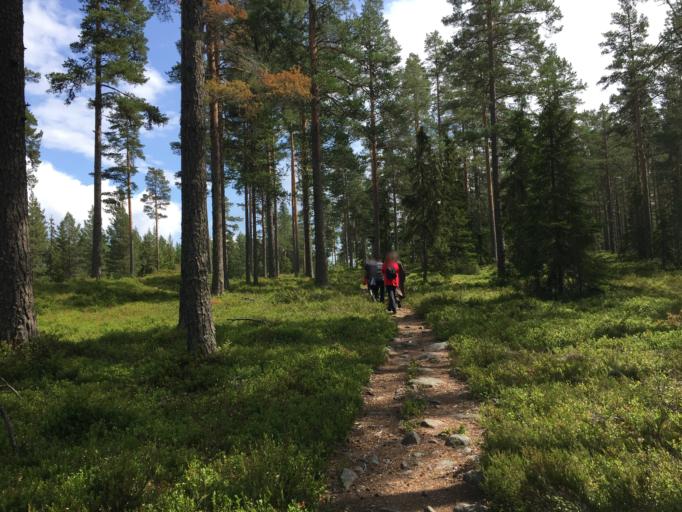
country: SE
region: Dalarna
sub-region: Malung-Saelens kommun
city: Malung
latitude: 60.6451
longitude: 13.7681
